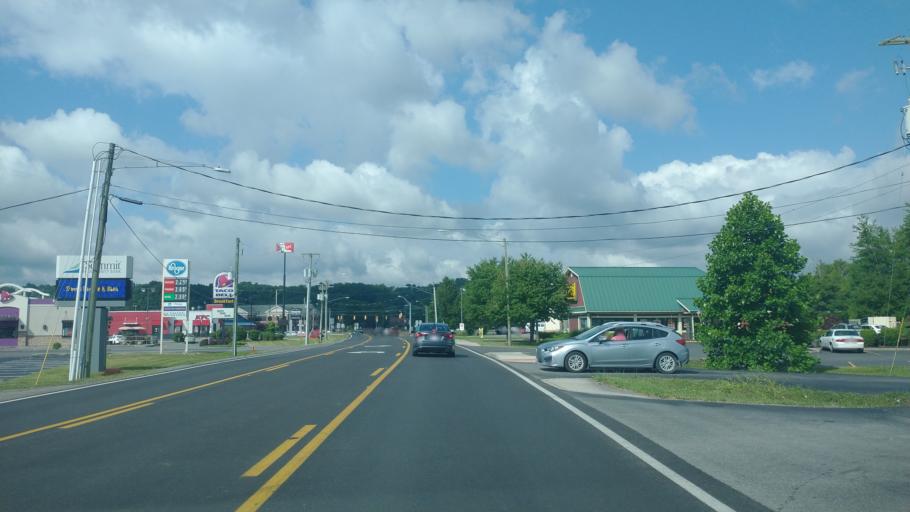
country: US
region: West Virginia
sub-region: Mercer County
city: Princeton
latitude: 37.3627
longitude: -81.0964
